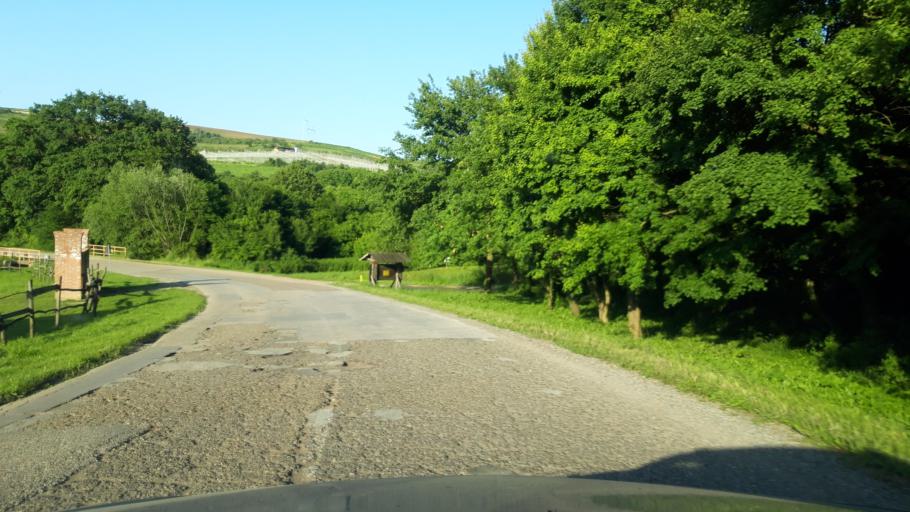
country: RS
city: Glozan
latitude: 45.1585
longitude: 19.5901
